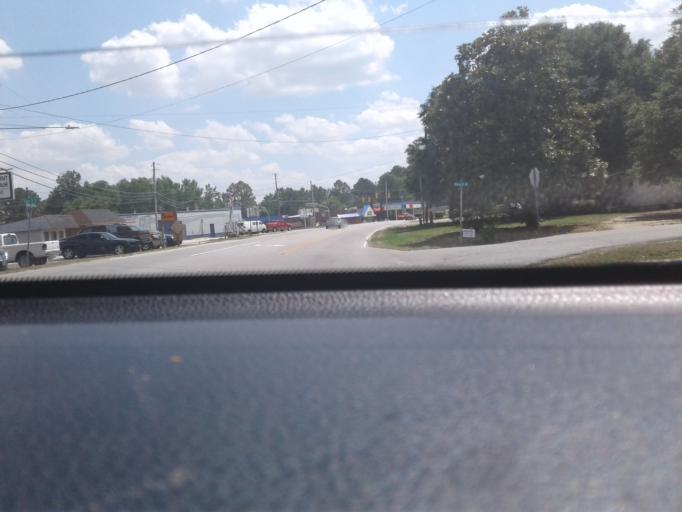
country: US
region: North Carolina
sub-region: Harnett County
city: Erwin
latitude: 35.3223
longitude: -78.6760
